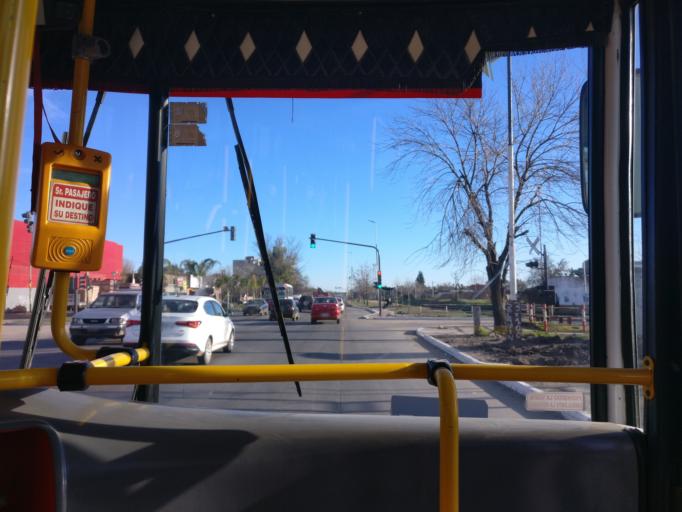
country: AR
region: Buenos Aires
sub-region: Partido de Ezeiza
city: Ezeiza
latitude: -34.8796
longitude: -58.5551
